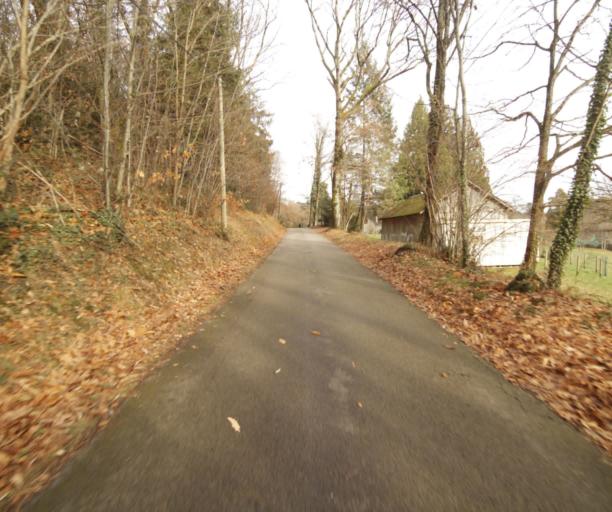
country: FR
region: Limousin
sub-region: Departement de la Correze
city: Saint-Mexant
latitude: 45.2583
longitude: 1.6658
